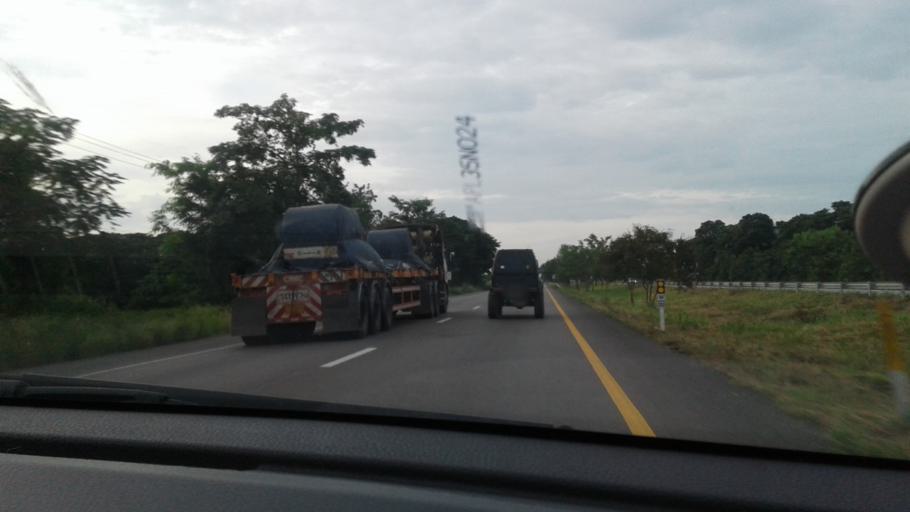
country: TH
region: Prachuap Khiri Khan
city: Pran Buri
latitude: 12.4431
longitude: 99.9082
